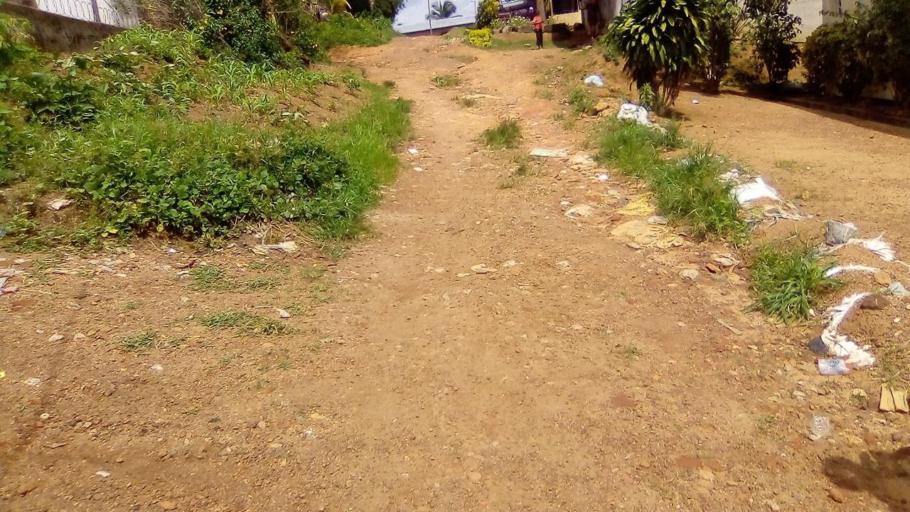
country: SL
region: Southern Province
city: Bo
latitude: 7.9675
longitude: -11.7304
